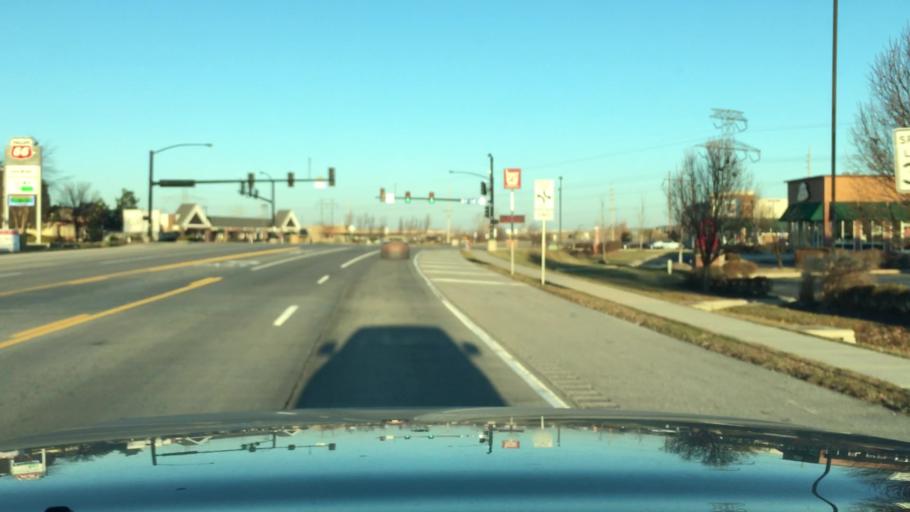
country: US
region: Missouri
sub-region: Saint Charles County
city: Saint Charles
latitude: 38.8207
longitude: -90.5152
